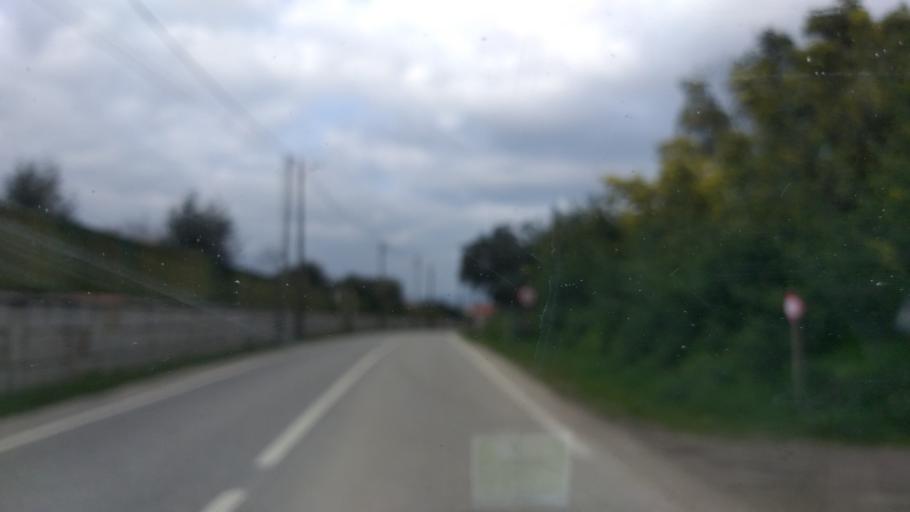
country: PT
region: Guarda
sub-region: Seia
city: Seia
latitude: 40.4889
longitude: -7.6324
